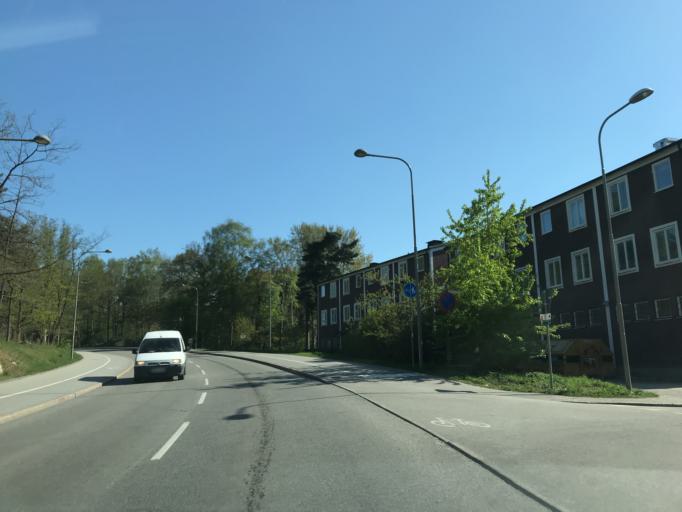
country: SE
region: Stockholm
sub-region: Stockholms Kommun
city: Arsta
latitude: 59.2909
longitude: 17.9995
